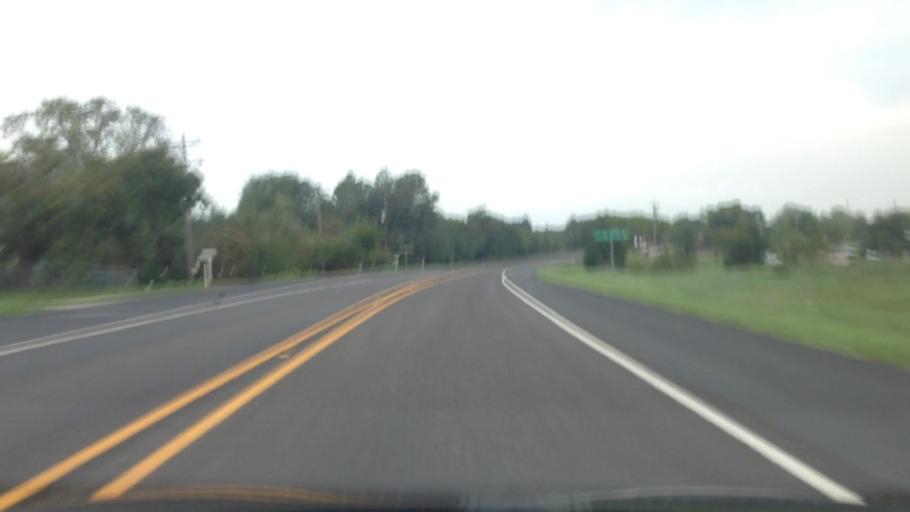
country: US
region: Texas
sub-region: Johnson County
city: Burleson
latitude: 32.4907
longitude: -97.3358
